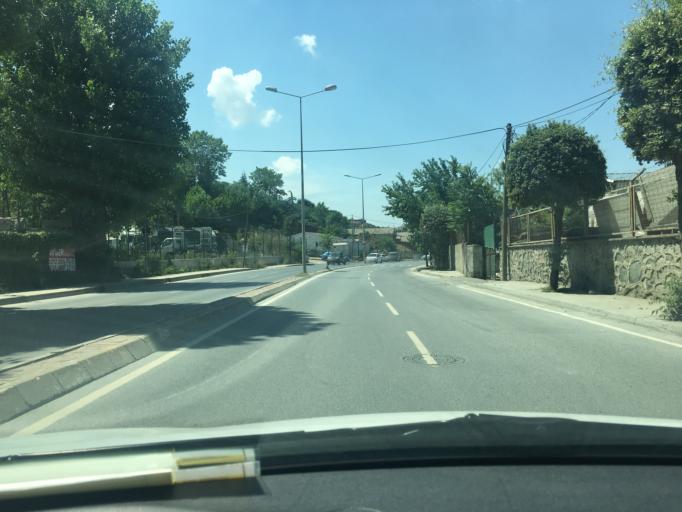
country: TR
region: Istanbul
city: Sisli
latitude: 41.0874
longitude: 28.9359
